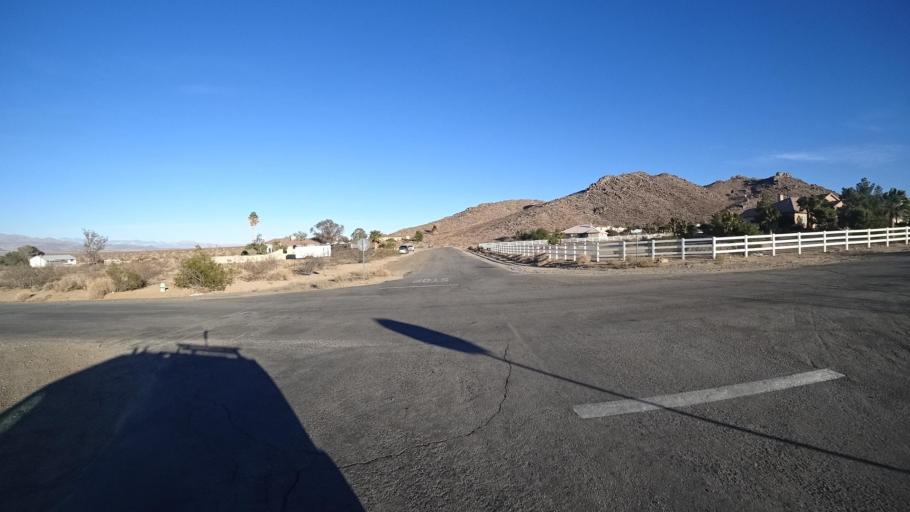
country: US
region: California
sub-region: Kern County
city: Ridgecrest
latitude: 35.5786
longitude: -117.6476
